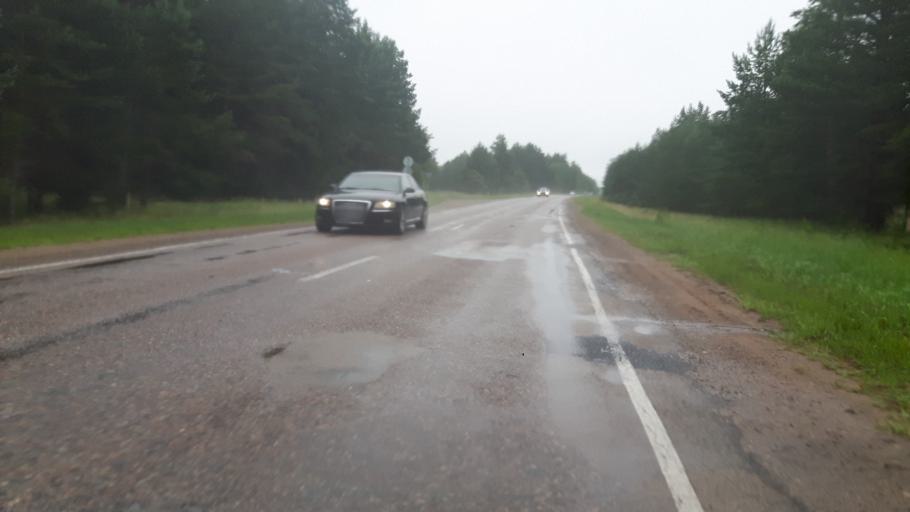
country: LT
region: Klaipedos apskritis
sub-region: Palanga
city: Sventoji
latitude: 56.0876
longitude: 21.1249
